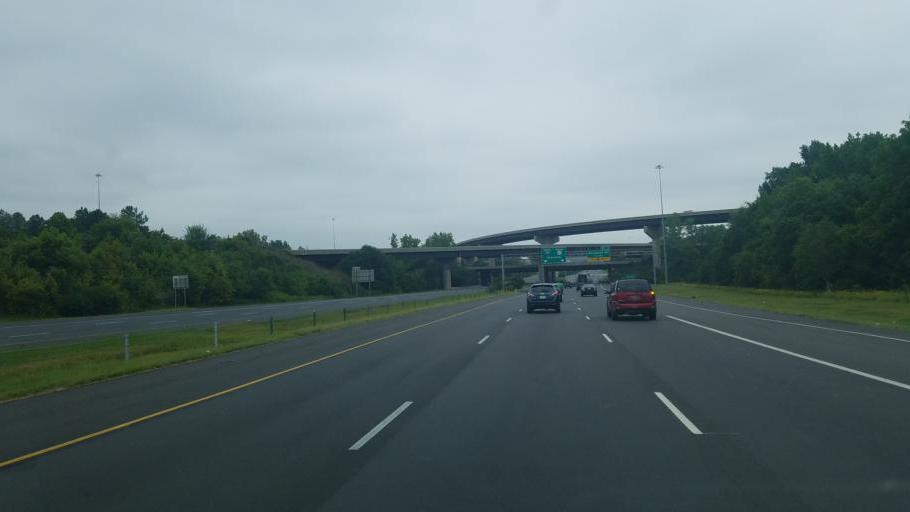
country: US
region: North Carolina
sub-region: Mecklenburg County
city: Pineville
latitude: 35.1227
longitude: -80.9191
